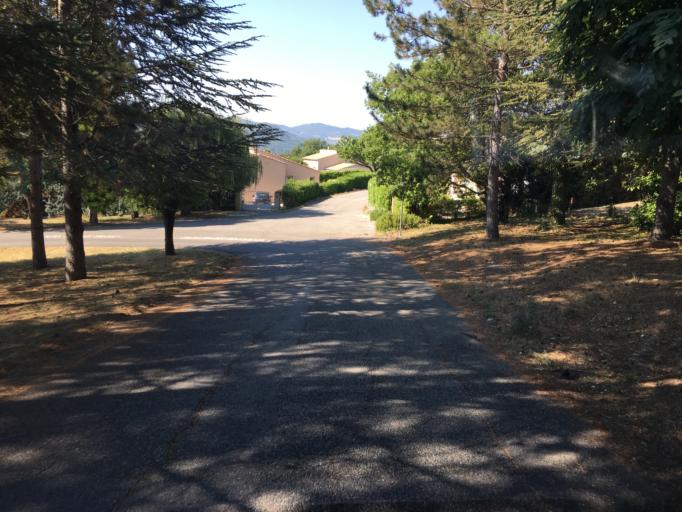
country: FR
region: Provence-Alpes-Cote d'Azur
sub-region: Departement des Alpes-de-Haute-Provence
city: Mallemoisson
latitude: 44.0526
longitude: 6.1410
